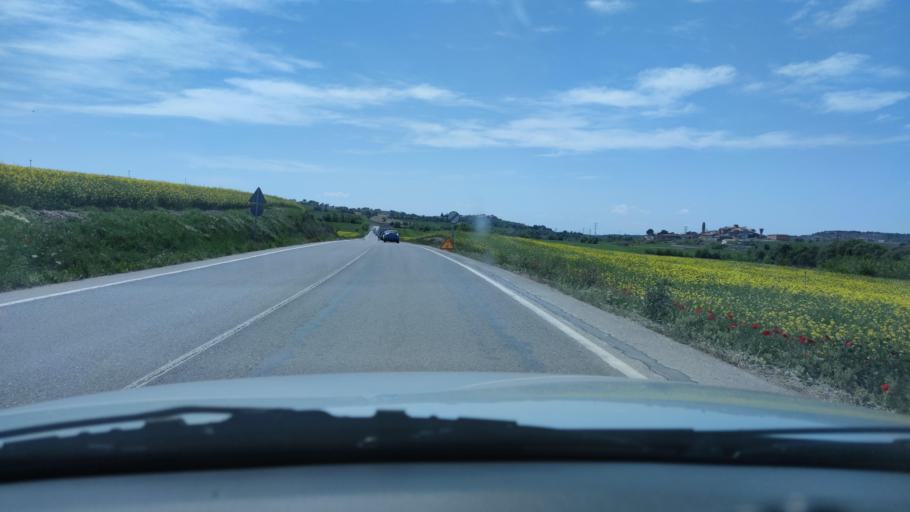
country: ES
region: Catalonia
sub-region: Provincia de Lleida
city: Mont-roig del Camp
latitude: 41.7777
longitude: 1.2678
